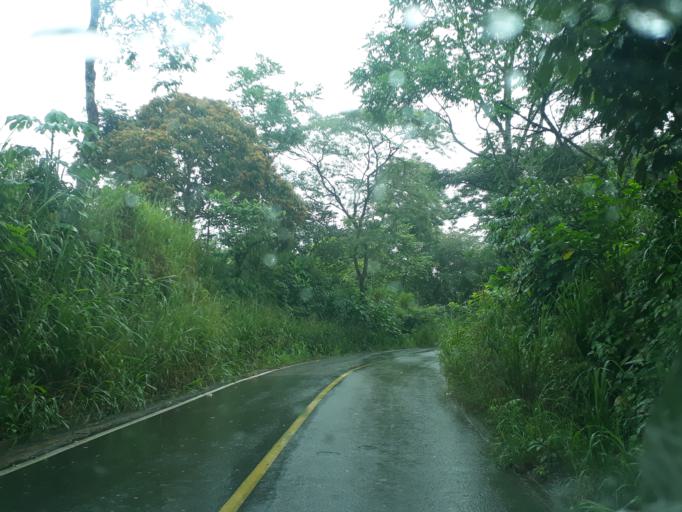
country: CO
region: Cundinamarca
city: Paratebueno
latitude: 4.3996
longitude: -73.3032
